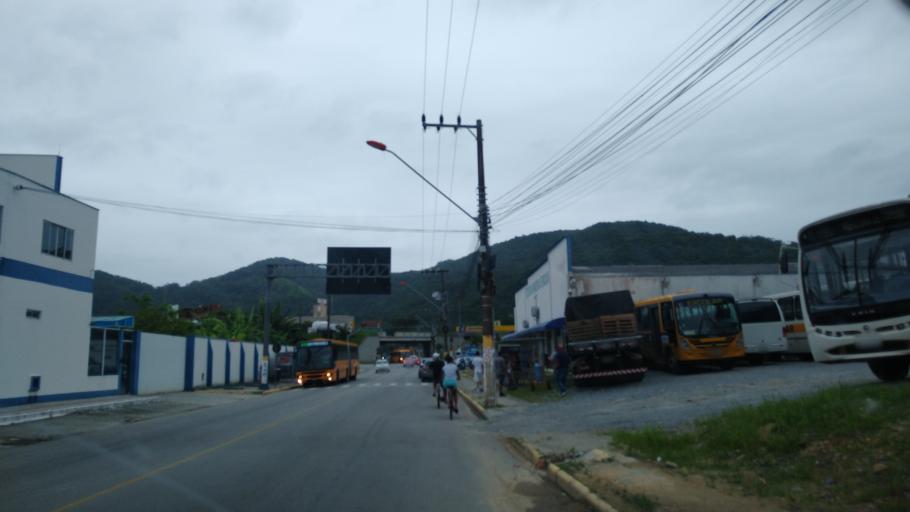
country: BR
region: Santa Catarina
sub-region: Itapema
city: Itapema
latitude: -27.0885
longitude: -48.6096
